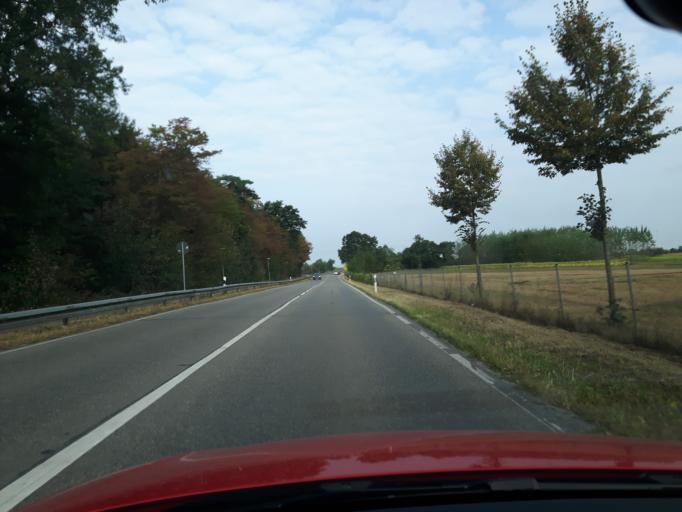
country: DE
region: Baden-Wuerttemberg
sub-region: Karlsruhe Region
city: Rheinstetten
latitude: 48.9657
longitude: 8.3348
